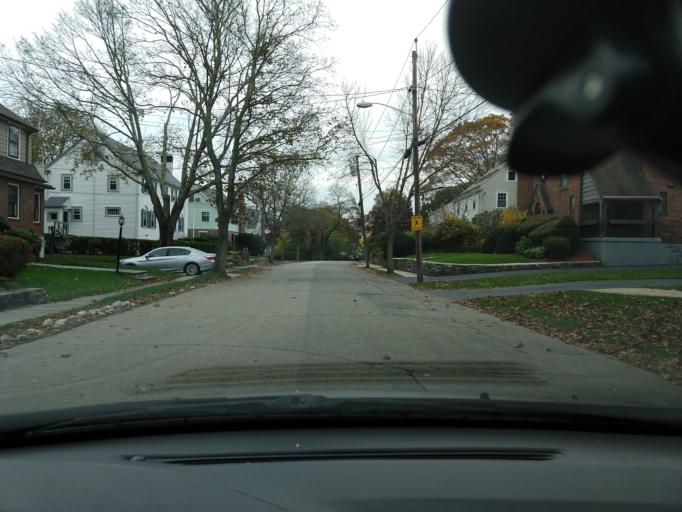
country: US
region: Massachusetts
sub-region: Middlesex County
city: Belmont
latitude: 42.4058
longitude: -71.1704
